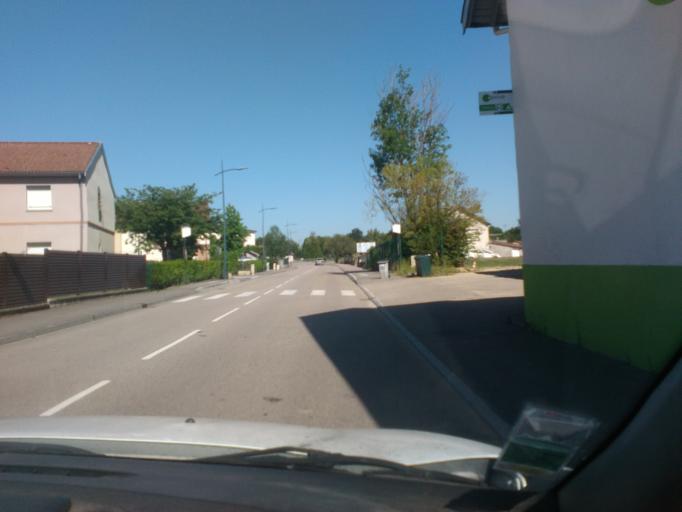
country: FR
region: Lorraine
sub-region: Departement des Vosges
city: Golbey
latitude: 48.2025
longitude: 6.4269
